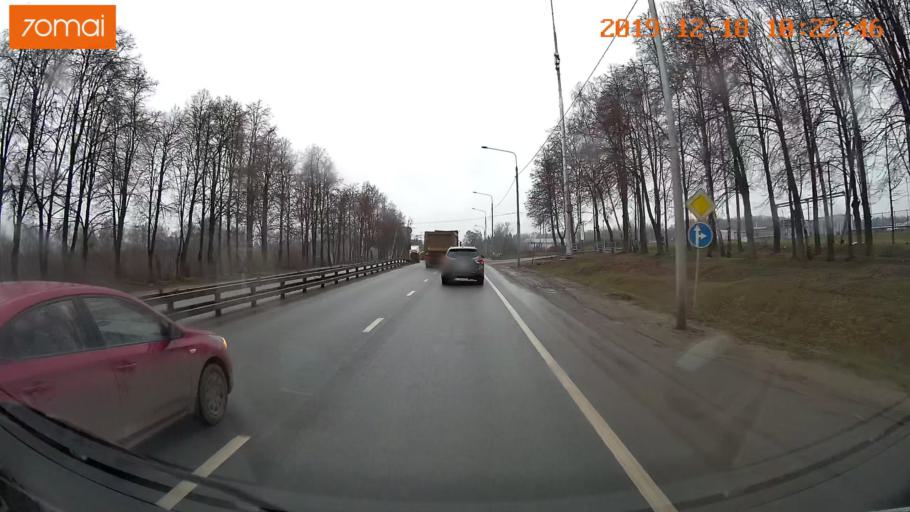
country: RU
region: Moskovskaya
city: Dubrovitsy
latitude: 55.3797
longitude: 37.4006
